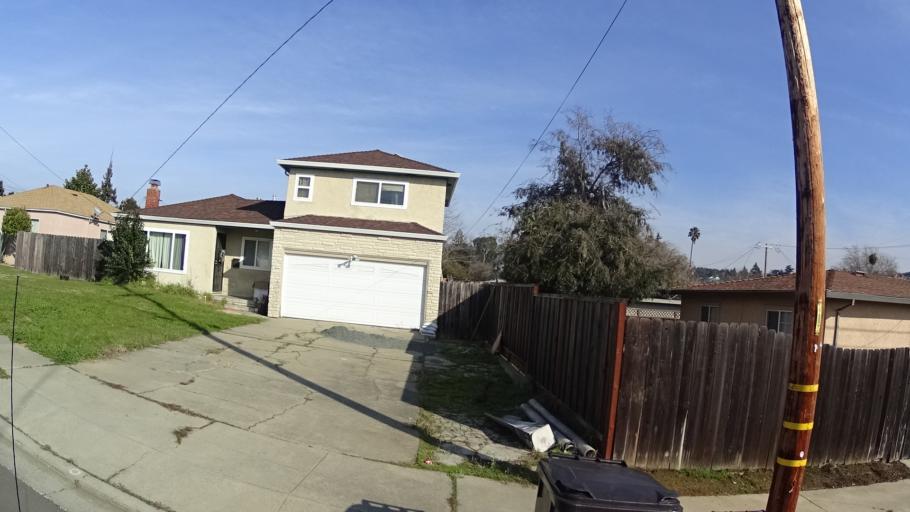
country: US
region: California
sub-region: Alameda County
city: Fairview
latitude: 37.6872
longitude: -122.0540
